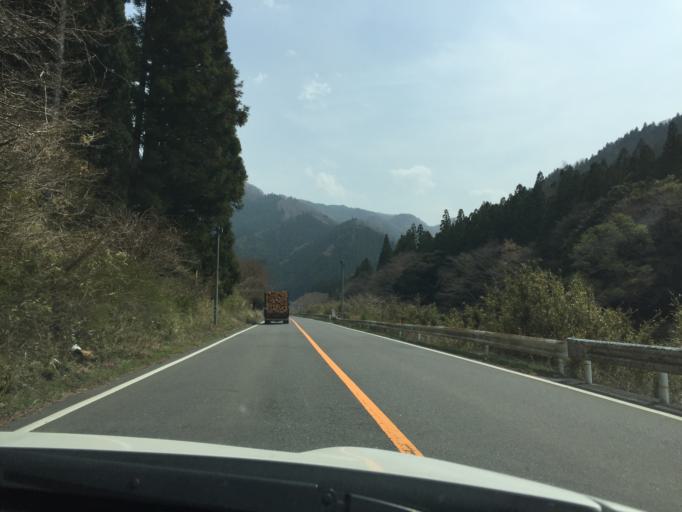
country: JP
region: Fukushima
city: Ishikawa
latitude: 37.0416
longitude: 140.6198
